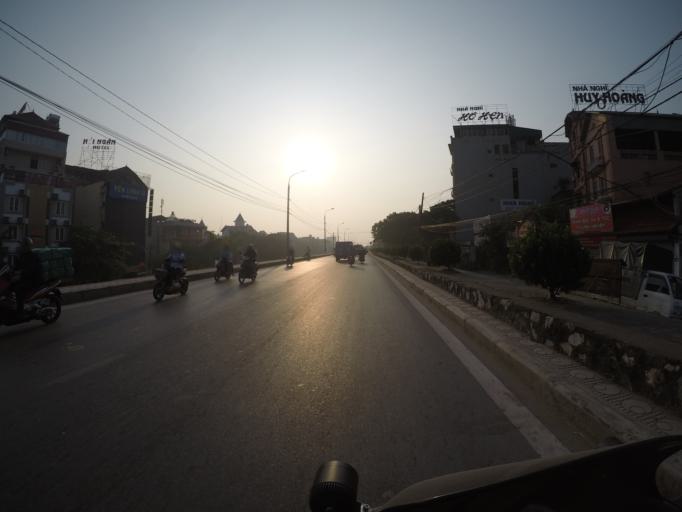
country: VN
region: Ha Noi
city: Hoan Kiem
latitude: 21.0383
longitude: 105.8679
